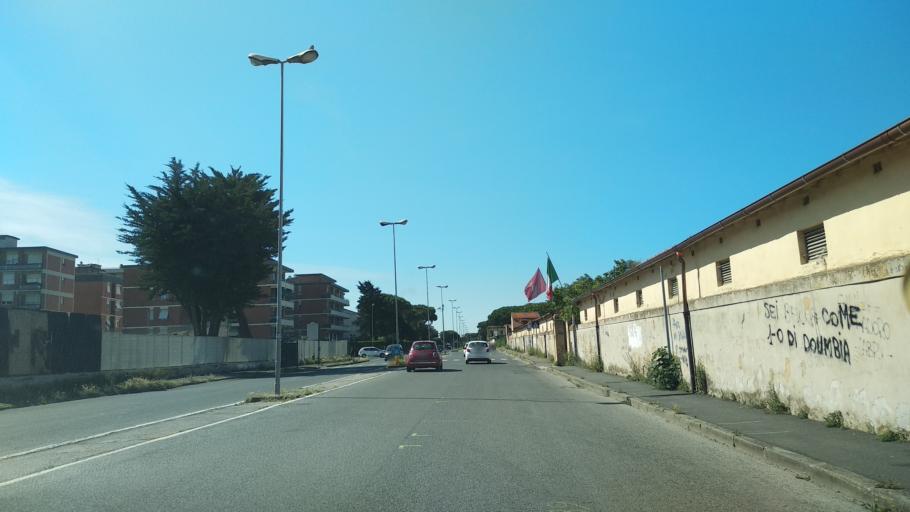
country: IT
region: Tuscany
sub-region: Provincia di Livorno
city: Livorno
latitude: 43.5241
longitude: 10.3159
